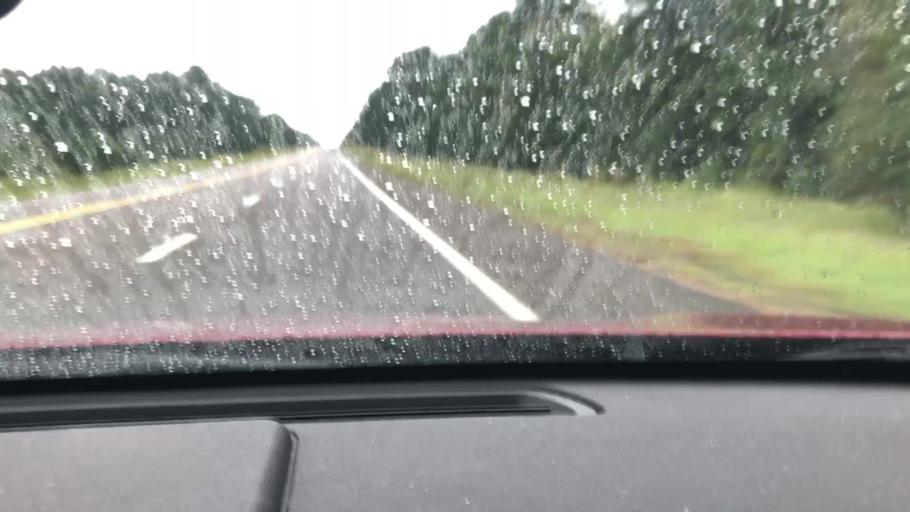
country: US
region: Arkansas
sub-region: Columbia County
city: Waldo
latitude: 33.3111
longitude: -93.2815
